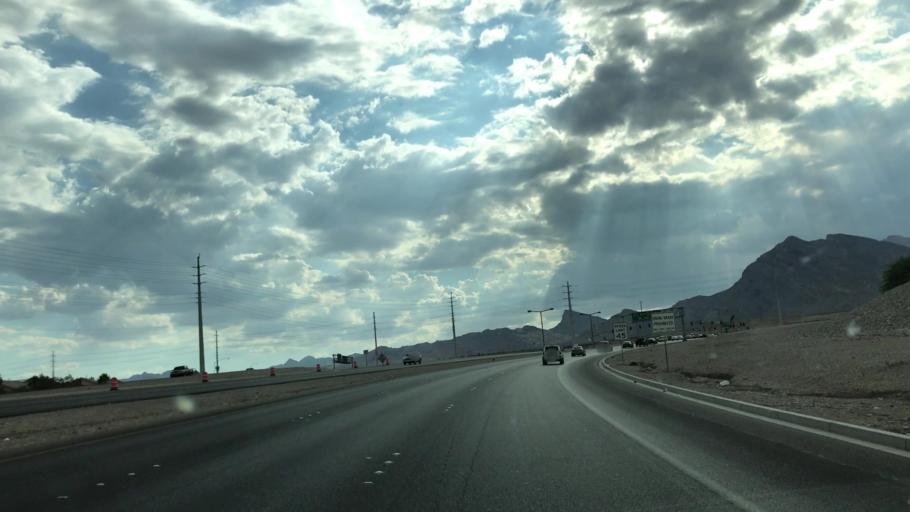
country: US
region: Nevada
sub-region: Clark County
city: Summerlin South
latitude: 36.1917
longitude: -115.3377
